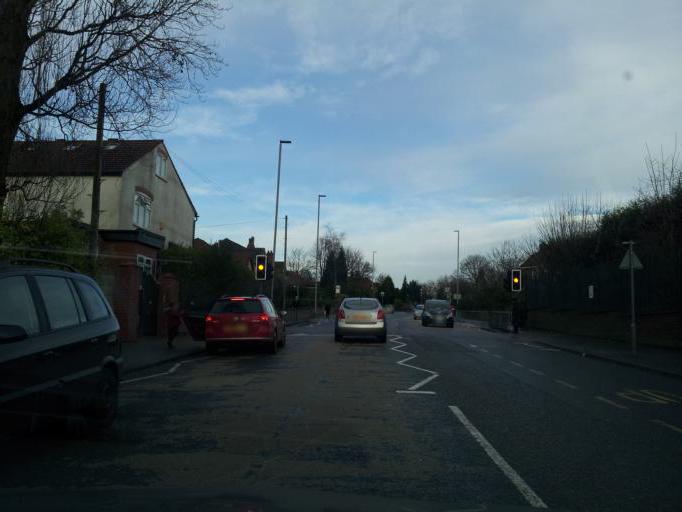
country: GB
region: England
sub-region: Manchester
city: Crumpsall
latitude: 53.5099
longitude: -2.2531
